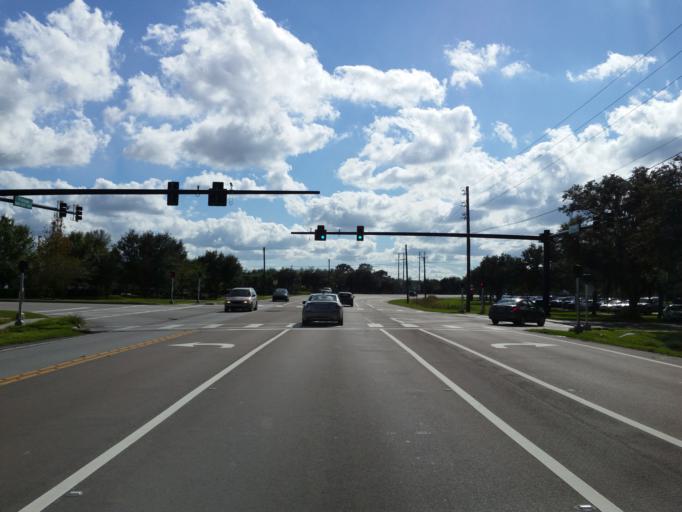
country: US
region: Florida
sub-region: Hillsborough County
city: Fish Hawk
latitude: 27.8573
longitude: -82.2047
